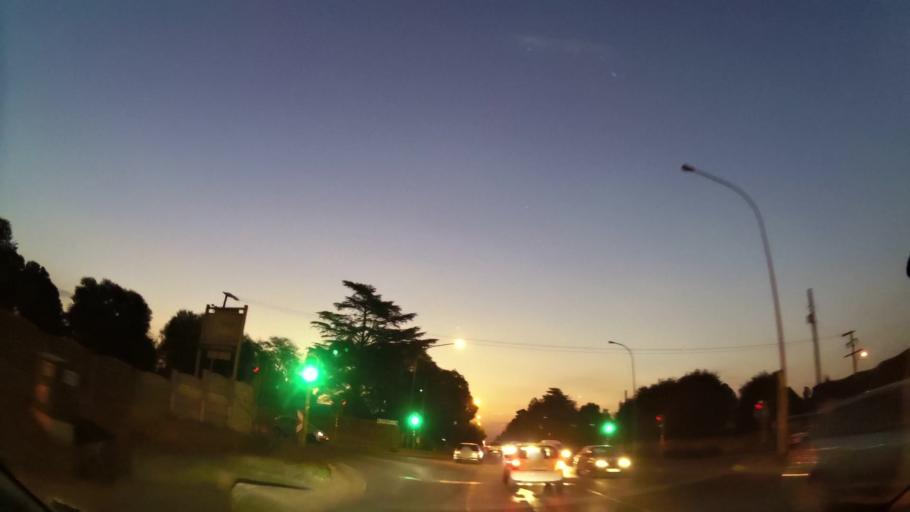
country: ZA
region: Gauteng
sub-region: Ekurhuleni Metropolitan Municipality
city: Benoni
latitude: -26.0909
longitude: 28.3023
